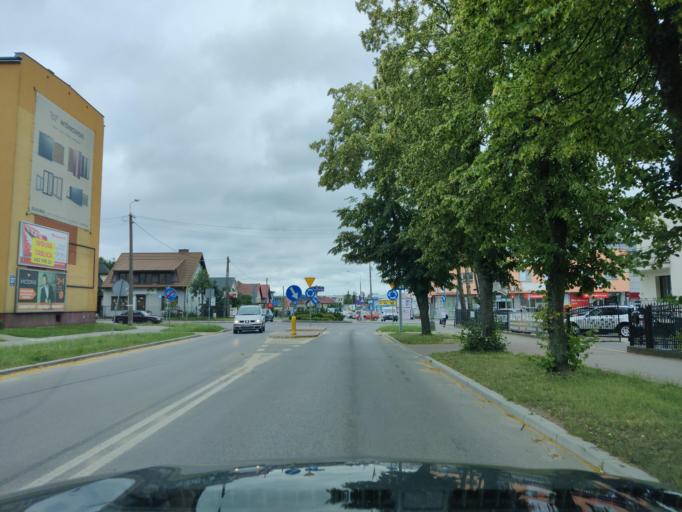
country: PL
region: Masovian Voivodeship
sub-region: Powiat pultuski
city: Pultusk
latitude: 52.7033
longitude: 21.0762
